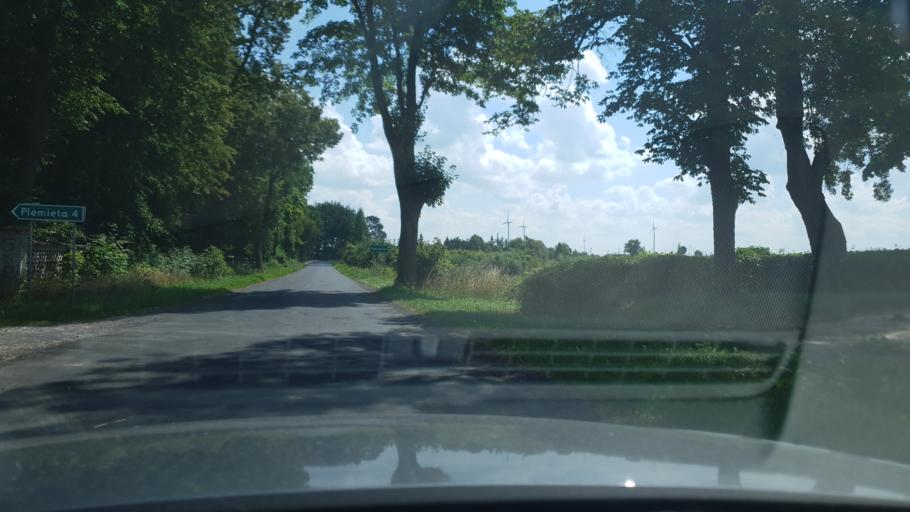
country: PL
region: Kujawsko-Pomorskie
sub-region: Powiat grudziadzki
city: Radzyn Chelminski
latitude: 53.3921
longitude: 18.8348
